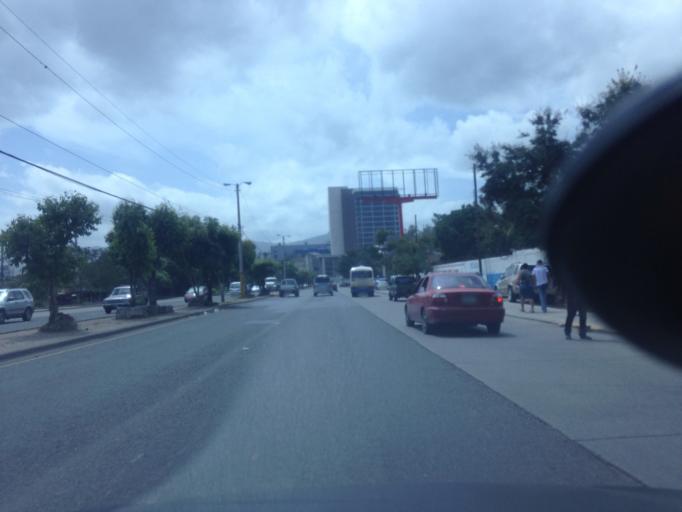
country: HN
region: Francisco Morazan
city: Tegucigalpa
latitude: 14.0720
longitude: -87.2097
